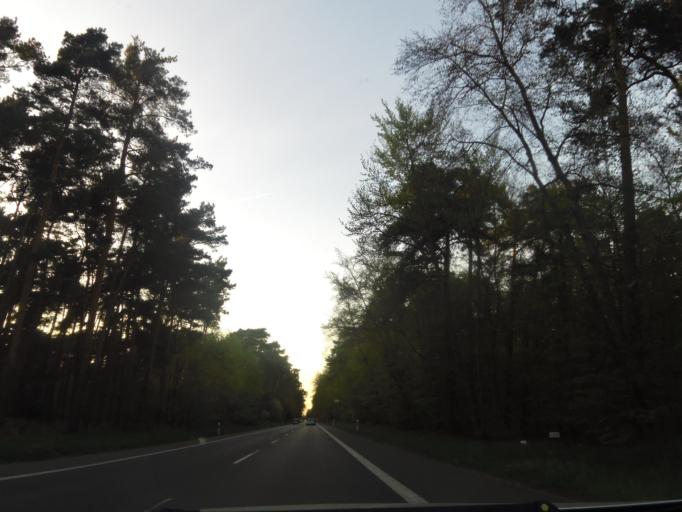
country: DE
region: Hesse
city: Weiterstadt
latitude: 49.9064
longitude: 8.6150
